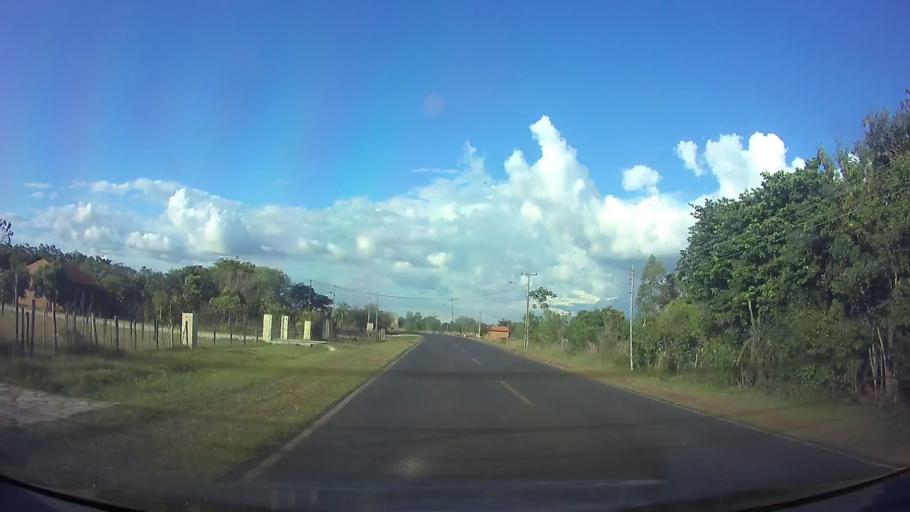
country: PY
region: Cordillera
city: Emboscada
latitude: -25.1586
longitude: -57.2634
